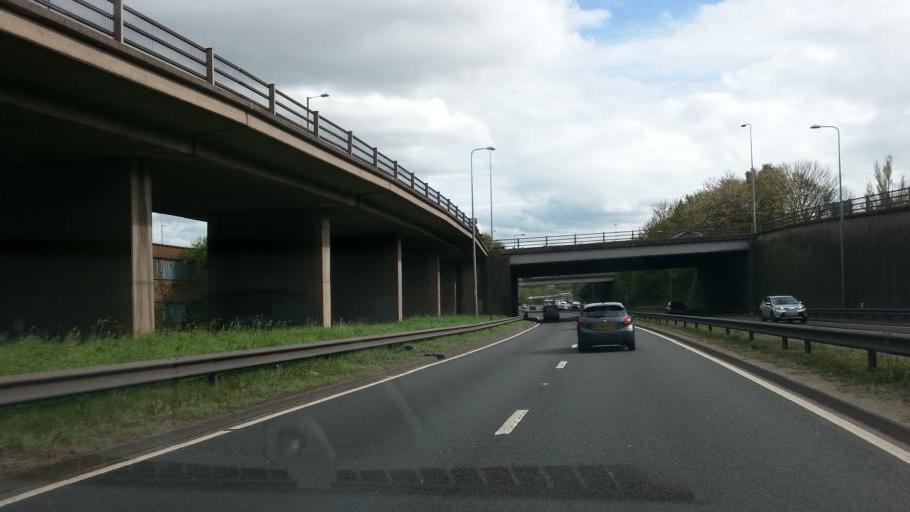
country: GB
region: England
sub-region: Stoke-on-Trent
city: Stoke-on-Trent
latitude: 53.0207
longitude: -2.2053
